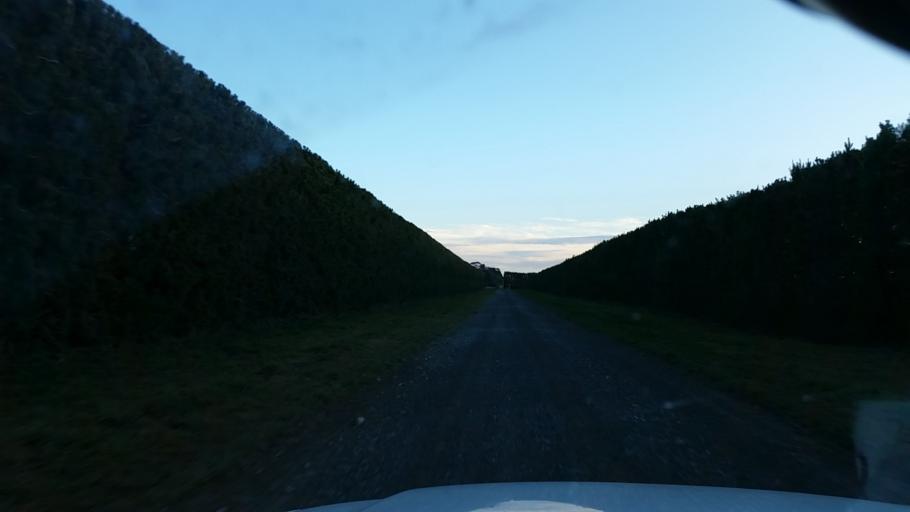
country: NZ
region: Canterbury
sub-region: Ashburton District
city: Tinwald
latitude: -43.9080
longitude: 171.5478
